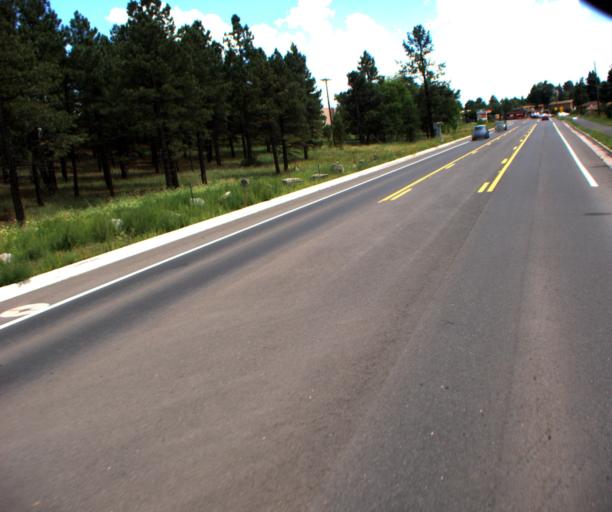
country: US
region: Arizona
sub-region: Coconino County
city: Flagstaff
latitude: 35.2095
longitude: -111.6488
